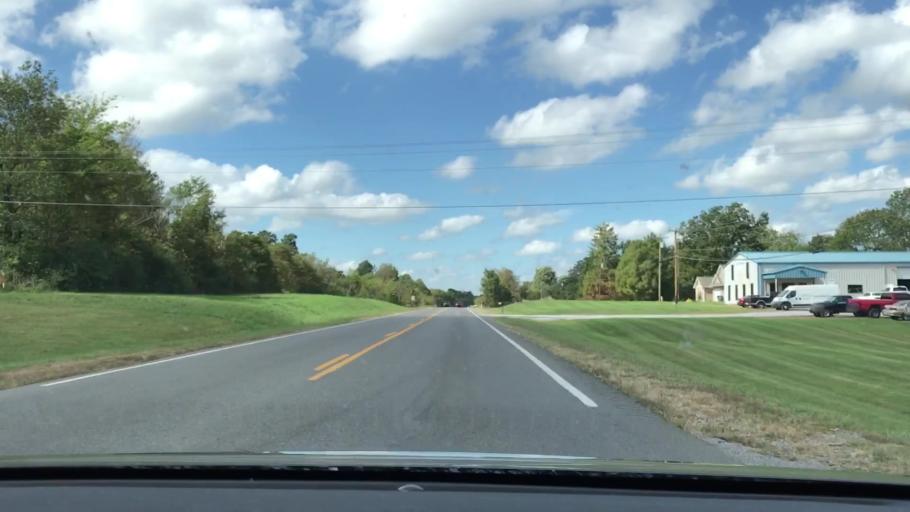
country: US
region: Kentucky
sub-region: McCracken County
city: Reidland
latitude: 37.0079
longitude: -88.4929
